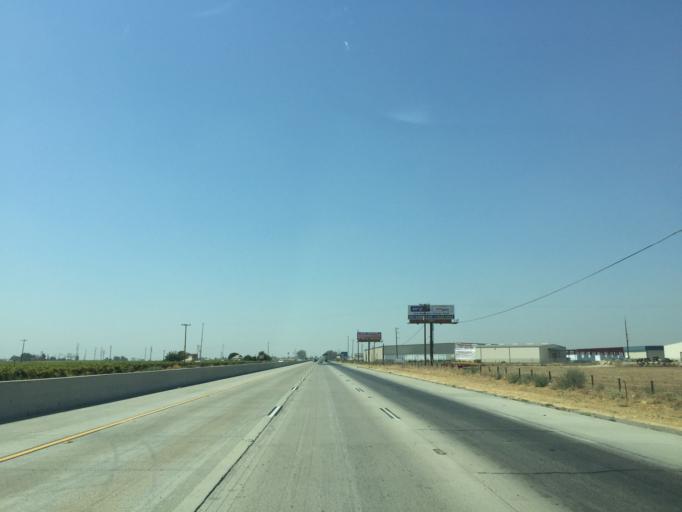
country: US
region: California
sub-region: Fresno County
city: Kingsburg
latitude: 36.5374
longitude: -119.5847
